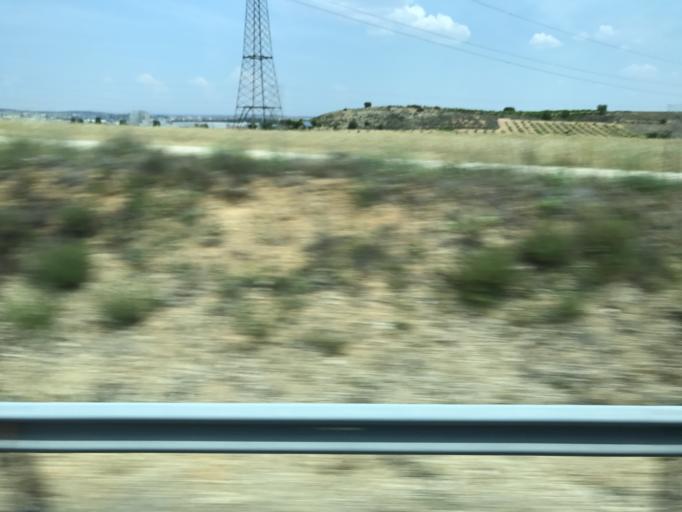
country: ES
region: Castille and Leon
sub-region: Provincia de Burgos
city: Fuentespina
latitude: 41.6458
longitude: -3.7154
